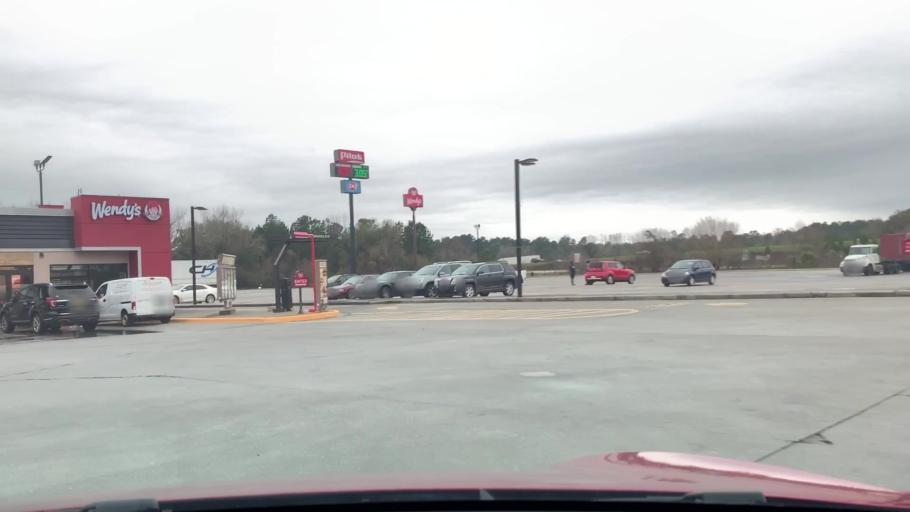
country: US
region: South Carolina
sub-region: Dorchester County
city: Saint George
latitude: 33.2700
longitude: -80.5670
